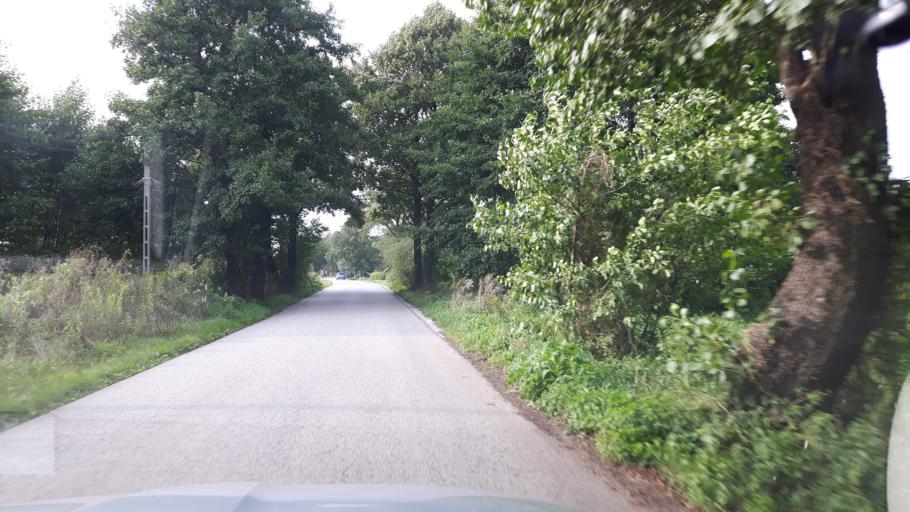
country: PL
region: Masovian Voivodeship
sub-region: Powiat wolominski
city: Marki
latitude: 52.3354
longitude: 21.0703
